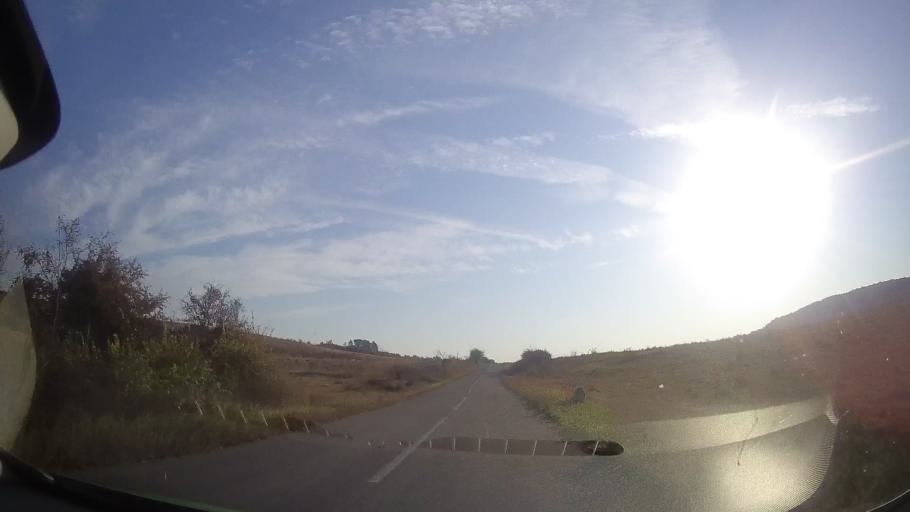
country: RO
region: Timis
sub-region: Comuna Bogda
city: Bogda
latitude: 45.9820
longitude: 21.5417
